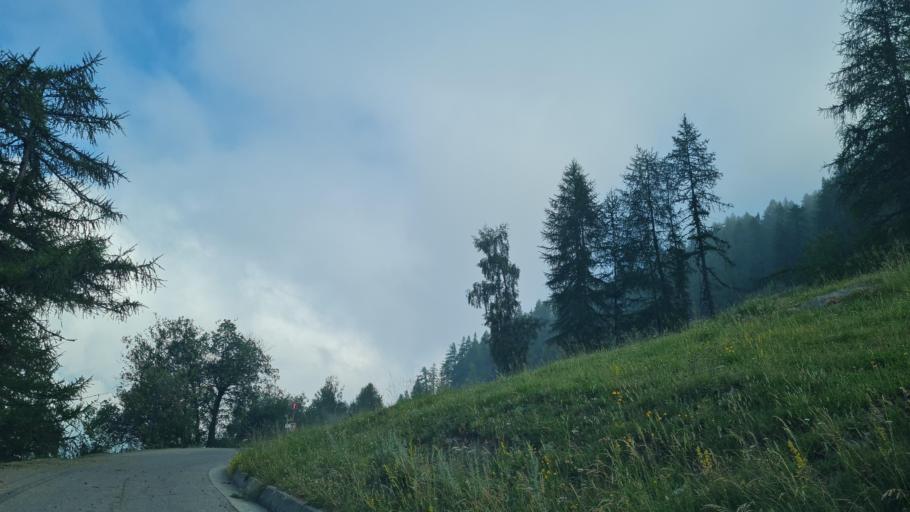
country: IT
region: Aosta Valley
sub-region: Valle d'Aosta
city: La Magdeleine
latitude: 45.8166
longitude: 7.6050
